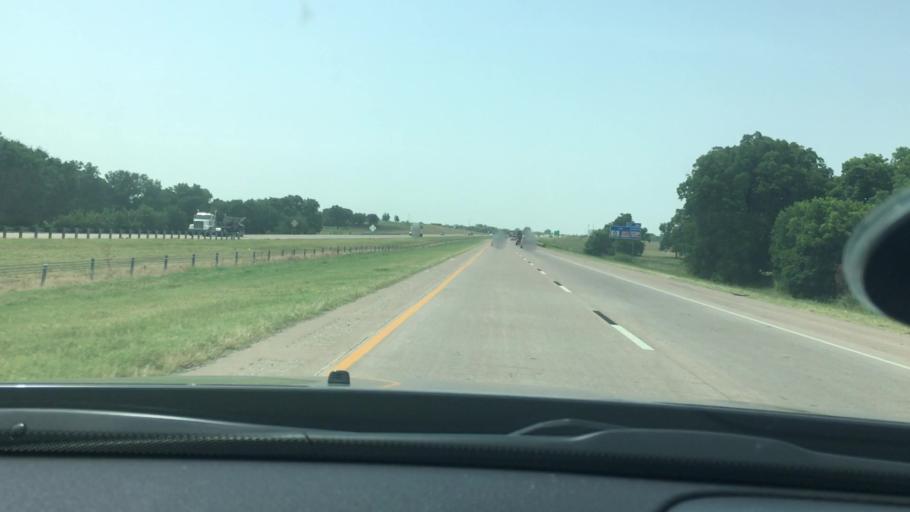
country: US
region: Oklahoma
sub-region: Garvin County
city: Wynnewood
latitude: 34.6653
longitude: -97.2231
